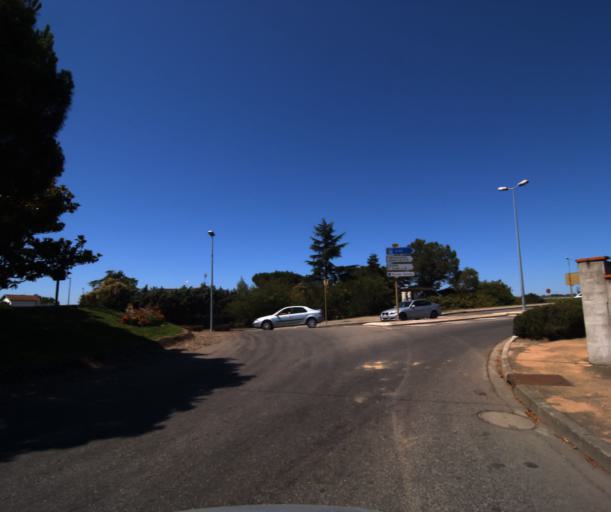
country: FR
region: Midi-Pyrenees
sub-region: Departement de la Haute-Garonne
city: Muret
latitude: 43.4646
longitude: 1.3164
